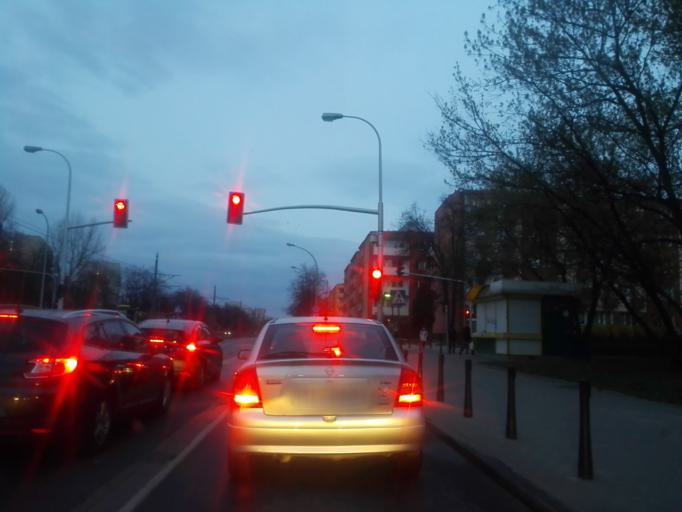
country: PL
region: Masovian Voivodeship
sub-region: Warszawa
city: Ochota
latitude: 52.2022
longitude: 20.9691
